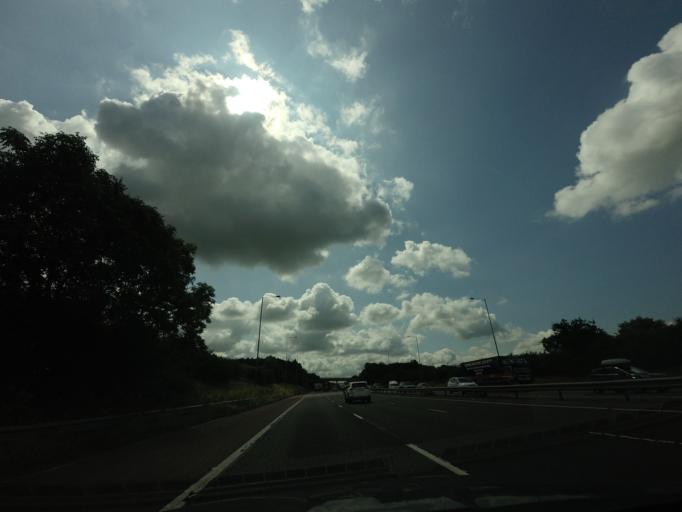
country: GB
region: England
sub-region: Lancashire
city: Euxton
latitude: 53.6531
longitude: -2.6909
